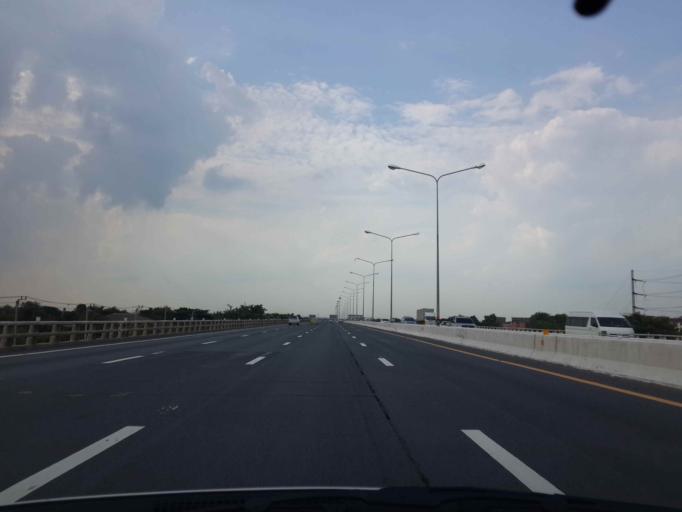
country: TH
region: Bangkok
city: Lat Krabang
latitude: 13.7118
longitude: 100.8192
